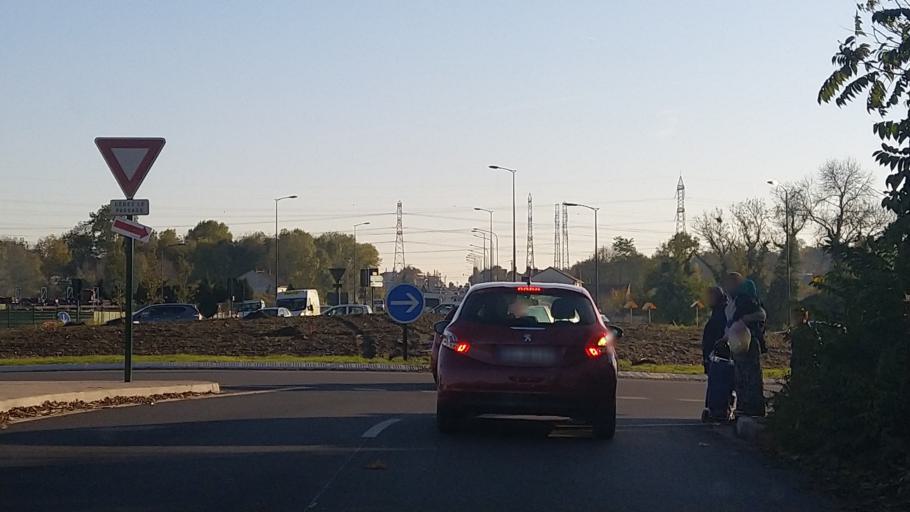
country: FR
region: Ile-de-France
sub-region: Departement du Val-d'Oise
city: Groslay
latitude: 48.9849
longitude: 2.3615
